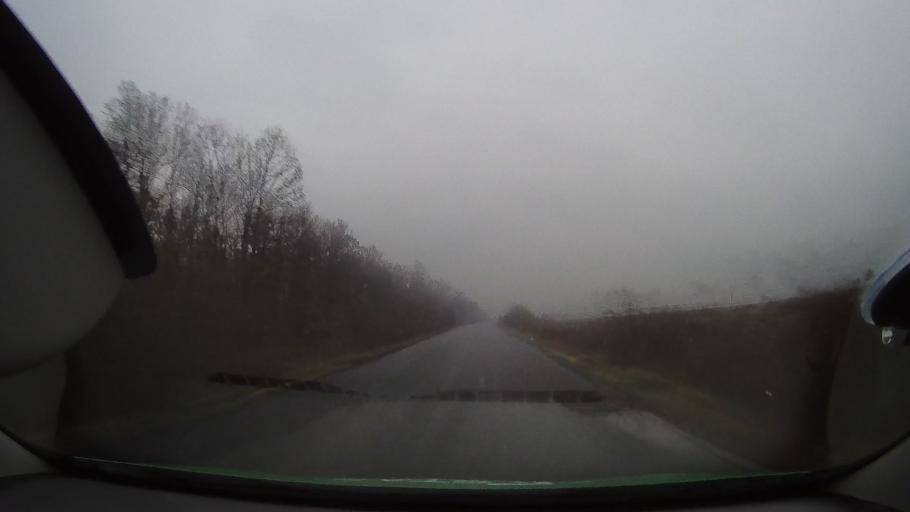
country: RO
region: Bihor
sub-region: Comuna Tinca
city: Gurbediu
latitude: 46.7789
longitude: 21.8754
